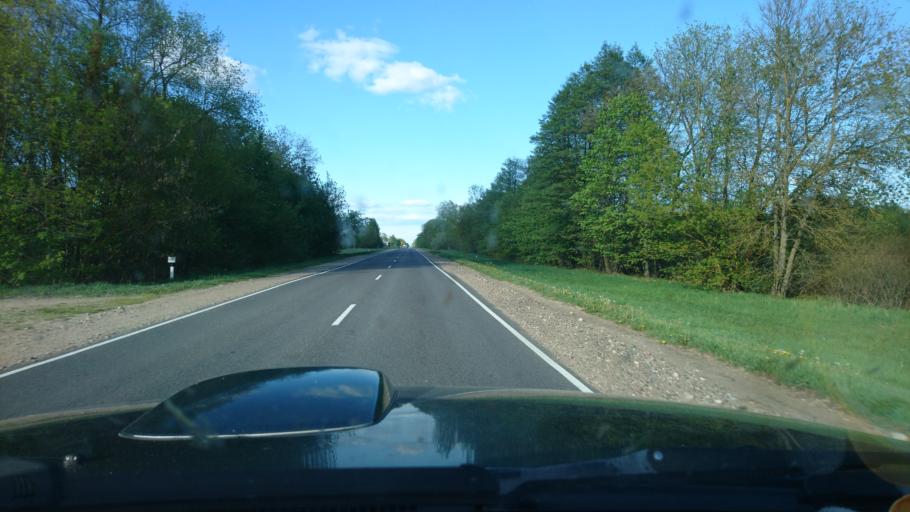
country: BY
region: Brest
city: Nyakhachava
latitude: 52.6419
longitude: 25.2014
